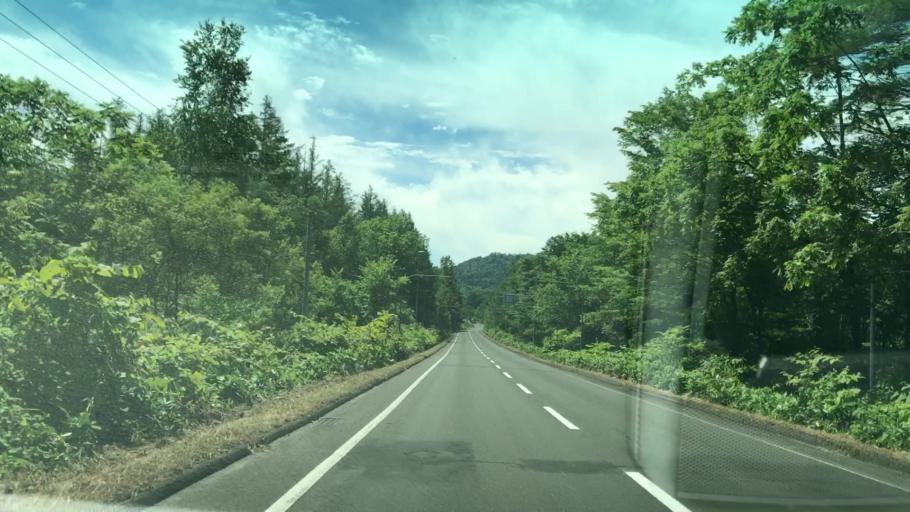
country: JP
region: Hokkaido
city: Shimo-furano
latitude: 42.9639
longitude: 142.4279
